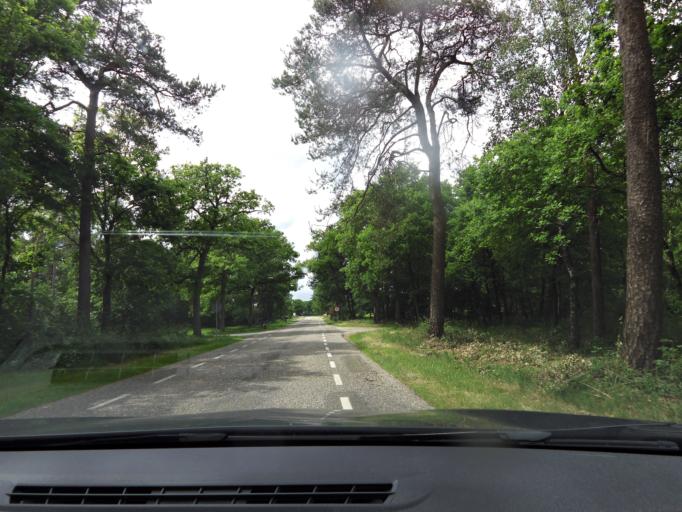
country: NL
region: Gelderland
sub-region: Gemeente Apeldoorn
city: Uddel
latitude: 52.2558
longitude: 5.7960
